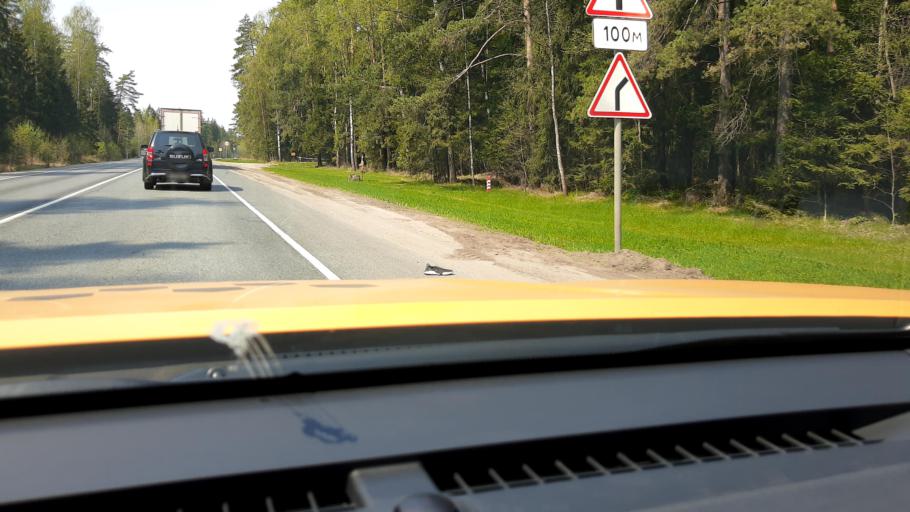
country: RU
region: Moskovskaya
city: Chernogolovka
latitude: 55.9873
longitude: 38.3341
